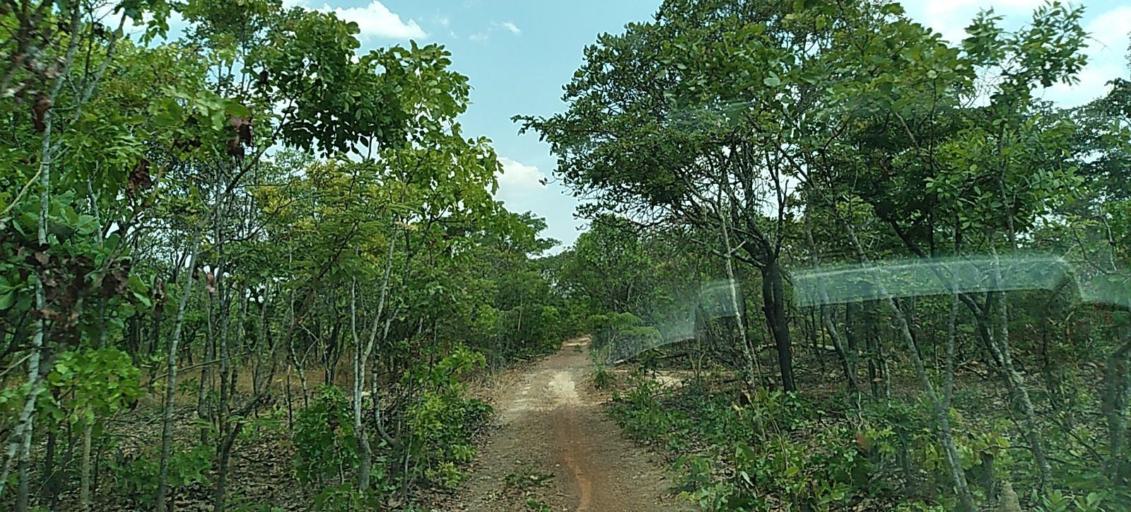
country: CD
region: Katanga
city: Kipushi
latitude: -11.9787
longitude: 27.4150
